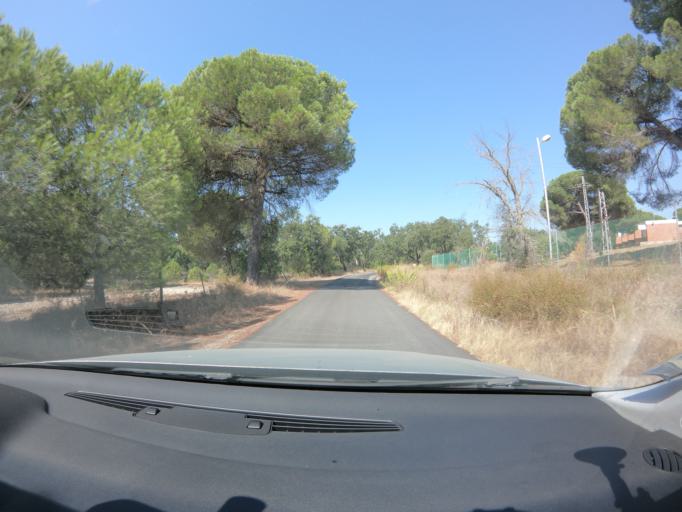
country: PT
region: Setubal
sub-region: Alcacer do Sal
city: Alcacer do Sal
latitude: 38.2660
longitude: -8.3156
